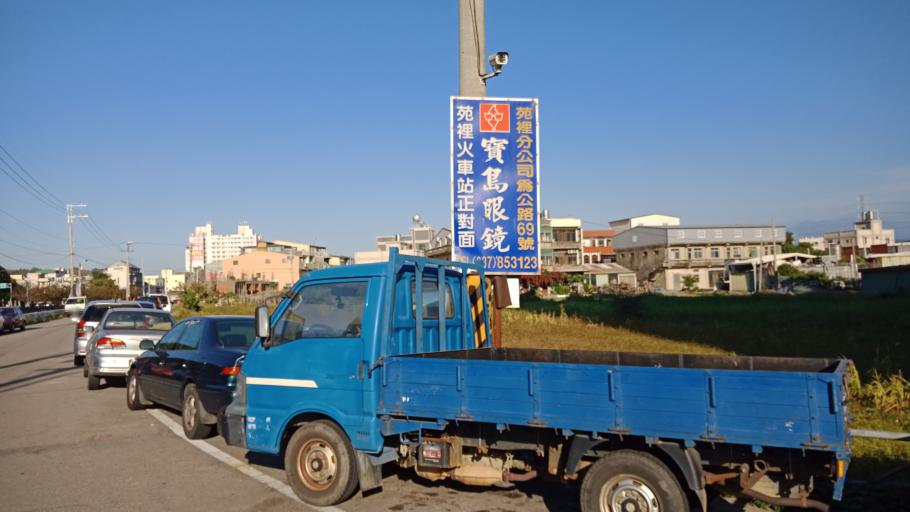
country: TW
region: Taiwan
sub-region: Miaoli
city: Miaoli
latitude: 24.4910
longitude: 120.6856
